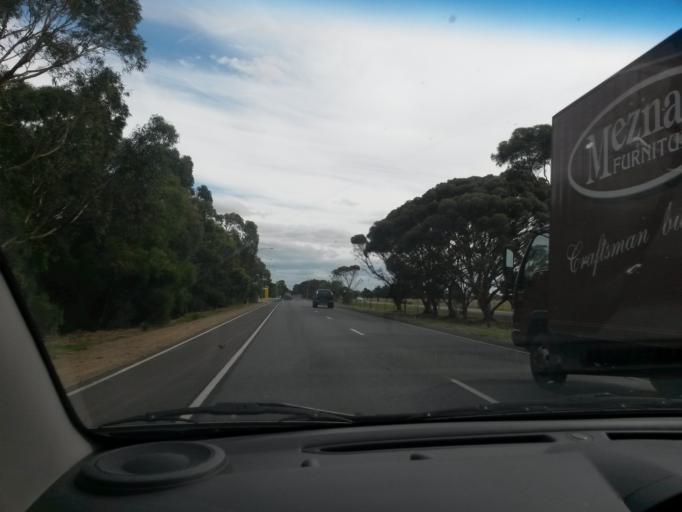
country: AU
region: South Australia
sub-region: Salisbury
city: Ingle Farm
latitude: -34.8029
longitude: 138.6373
